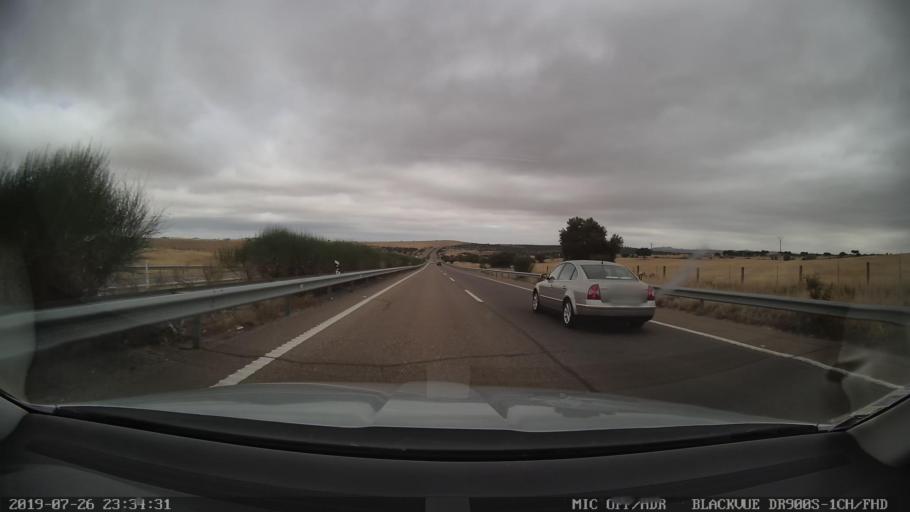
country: ES
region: Extremadura
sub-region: Provincia de Caceres
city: Santa Cruz de la Sierra
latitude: 39.3610
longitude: -5.8672
